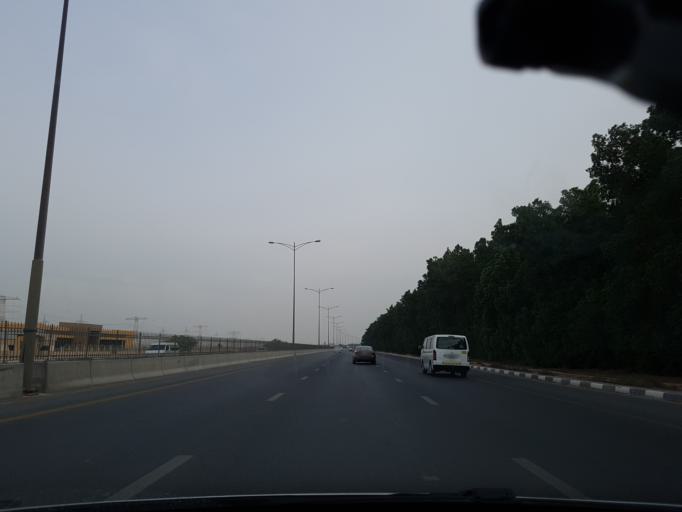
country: AE
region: Ajman
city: Ajman
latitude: 25.3656
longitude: 55.4695
